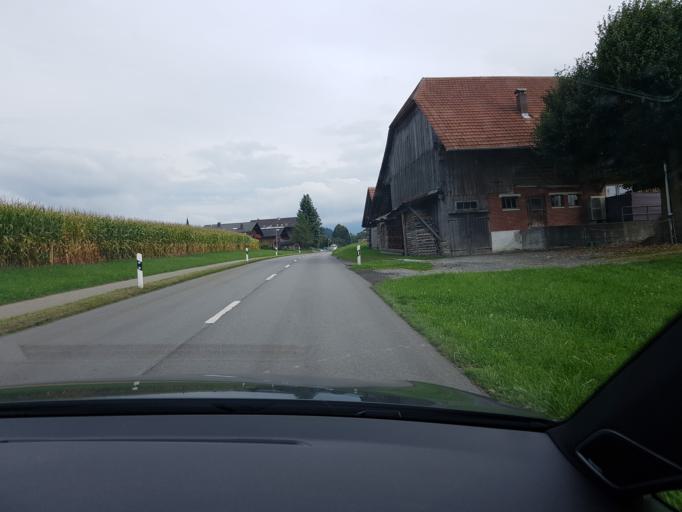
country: CH
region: Bern
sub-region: Thun District
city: Buchholterberg
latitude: 46.7966
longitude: 7.7063
